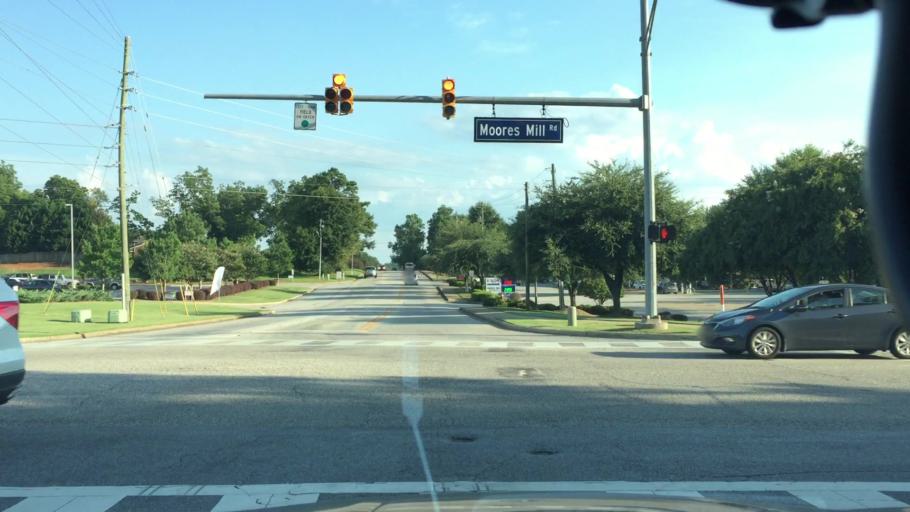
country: US
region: Alabama
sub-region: Lee County
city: Auburn
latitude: 32.5847
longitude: -85.4390
